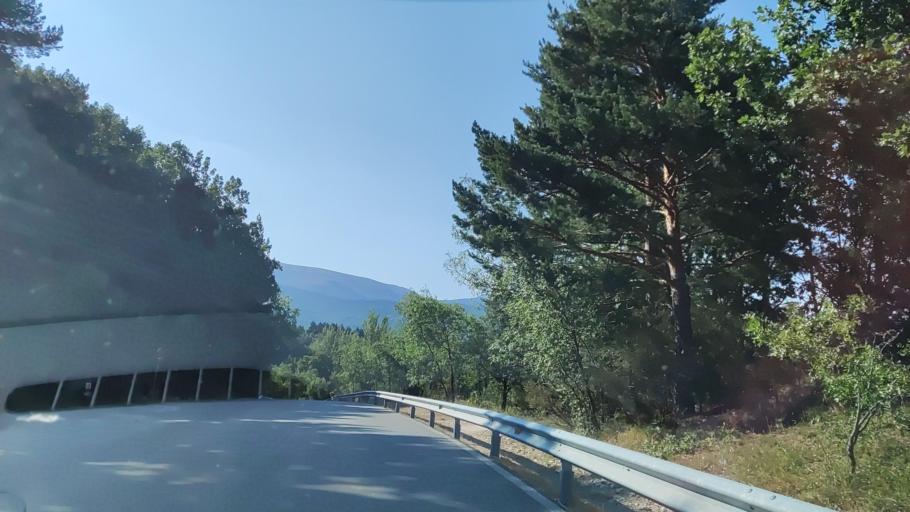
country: ES
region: Madrid
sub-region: Provincia de Madrid
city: Rascafria
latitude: 40.8817
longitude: -3.8854
